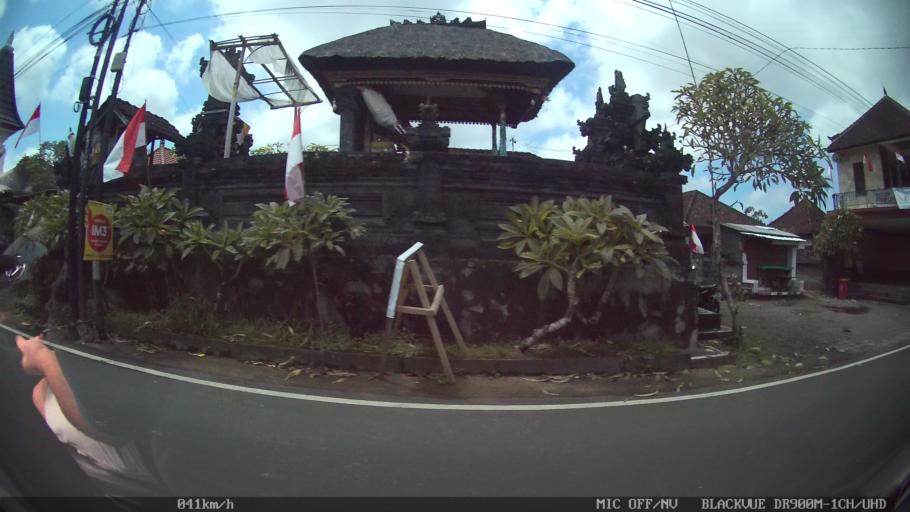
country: ID
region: Bali
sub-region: Kabupaten Gianyar
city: Ubud
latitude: -8.5358
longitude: 115.2822
